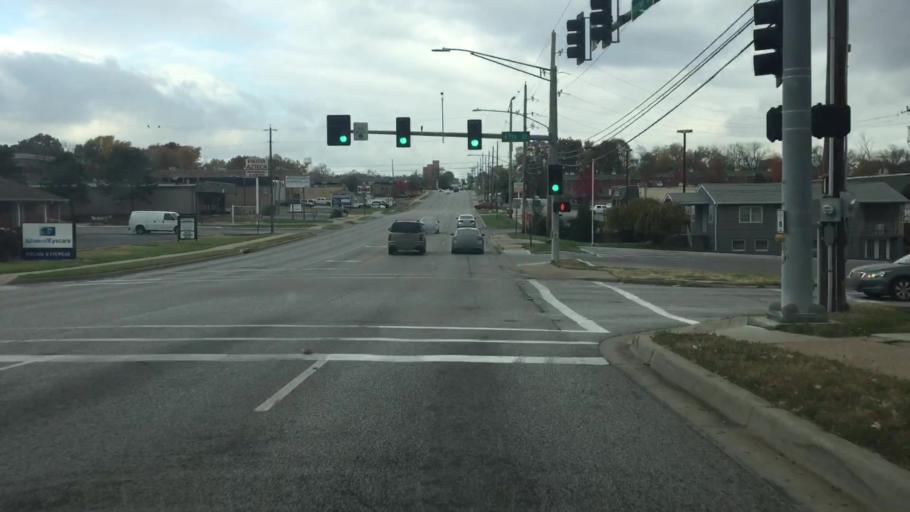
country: US
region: Missouri
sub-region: Jackson County
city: Raytown
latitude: 39.0009
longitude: -94.4637
